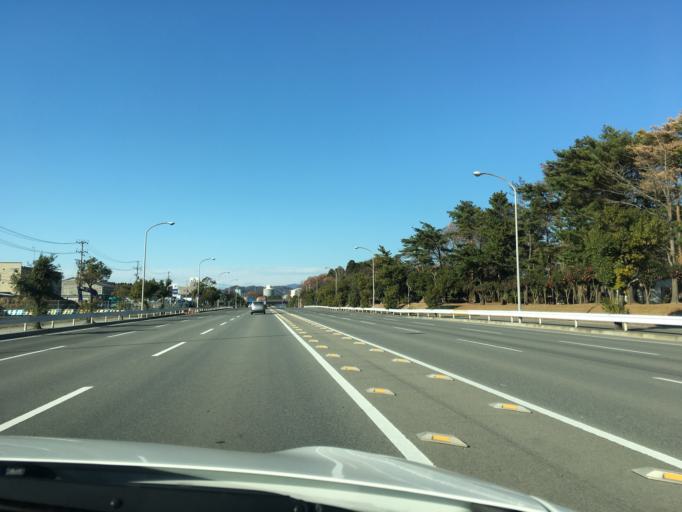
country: JP
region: Fukushima
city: Iwaki
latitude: 36.9342
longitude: 140.8593
